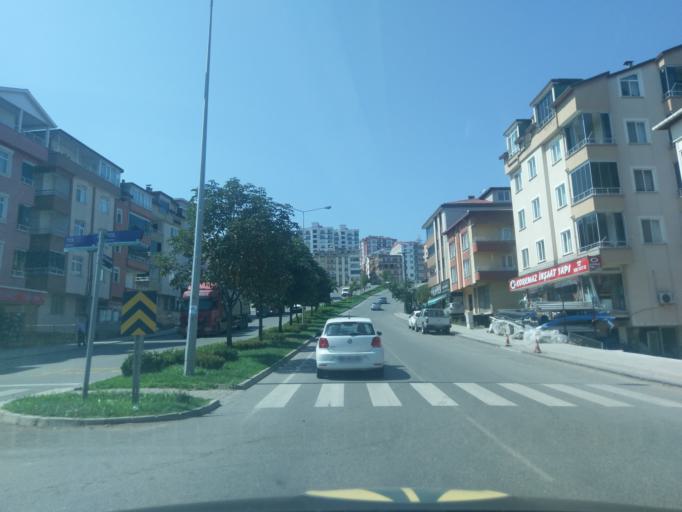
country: TR
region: Ordu
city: Ordu
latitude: 40.9662
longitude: 37.9026
